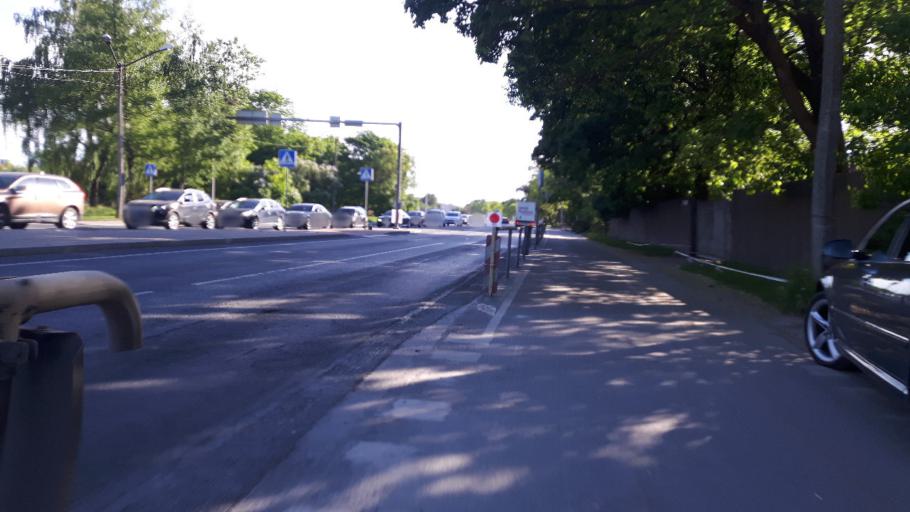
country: EE
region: Harju
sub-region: Viimsi vald
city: Viimsi
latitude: 59.4459
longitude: 24.8177
